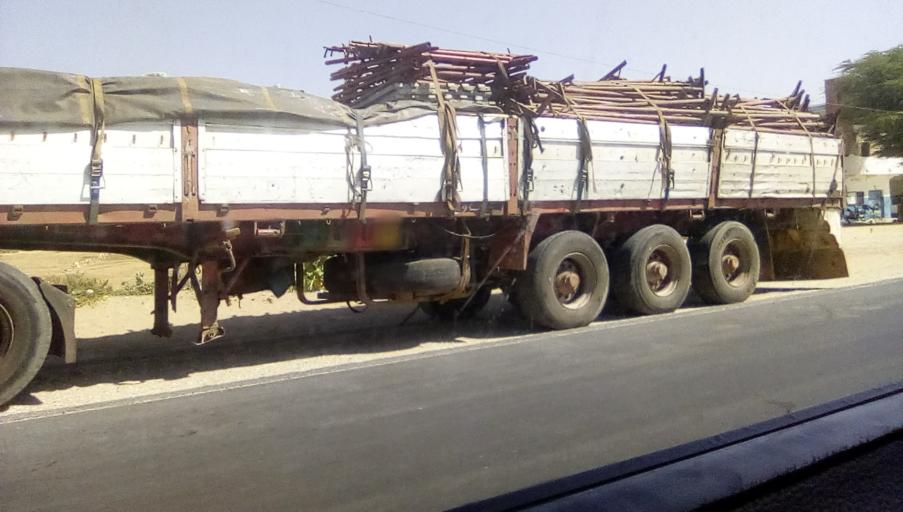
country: SN
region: Saint-Louis
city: Saint-Louis
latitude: 16.0454
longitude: -16.4367
